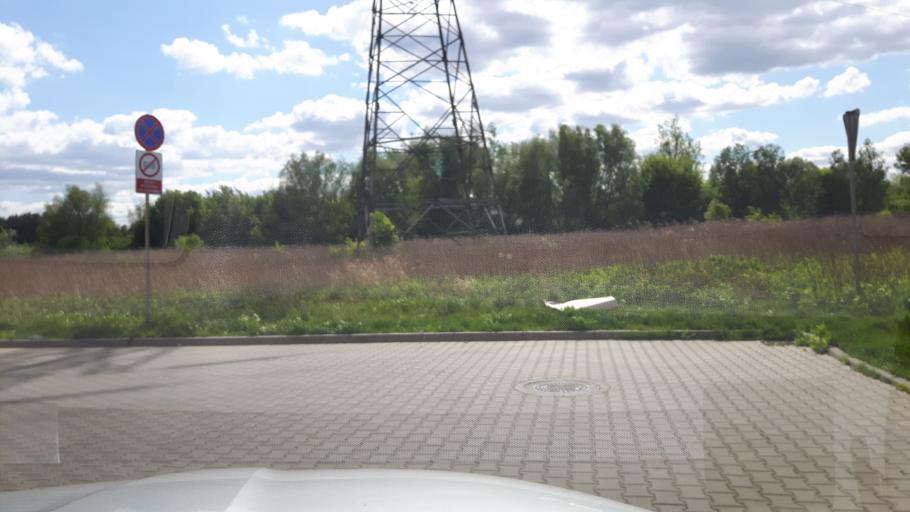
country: PL
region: Masovian Voivodeship
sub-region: Warszawa
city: Targowek
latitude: 52.3048
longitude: 21.0722
